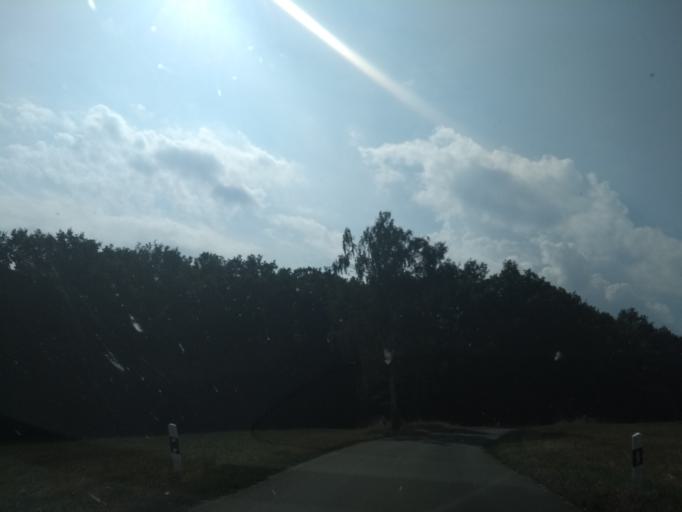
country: DE
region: Thuringia
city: Walpernhain
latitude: 51.0059
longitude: 11.9550
